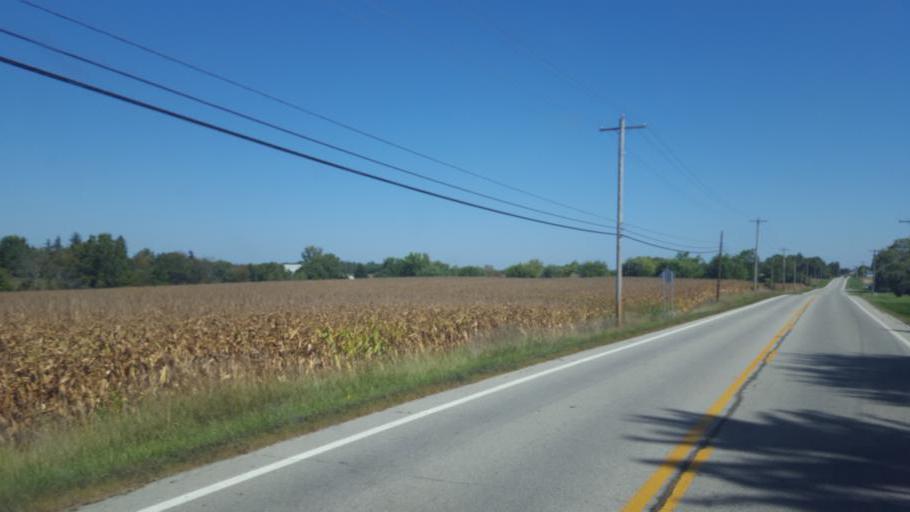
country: US
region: Ohio
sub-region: Crawford County
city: Crestline
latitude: 40.7454
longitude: -82.7429
